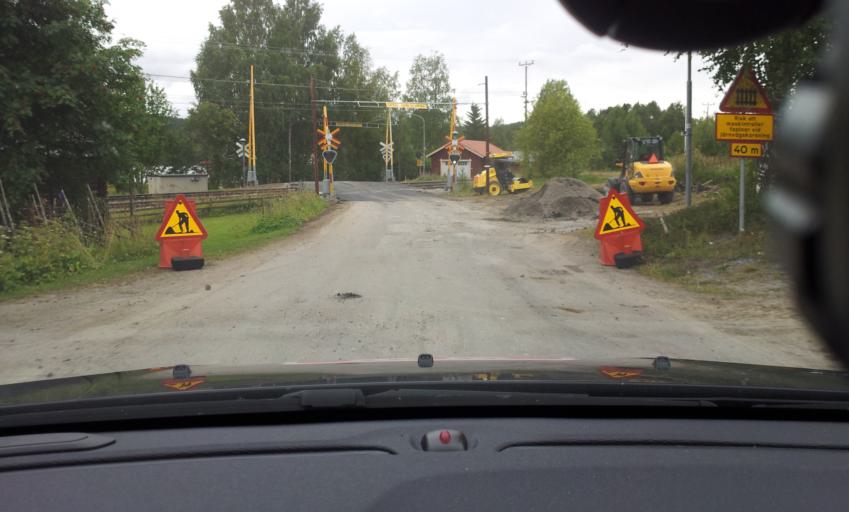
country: SE
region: Jaemtland
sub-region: OEstersunds Kommun
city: Brunflo
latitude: 62.9574
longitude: 15.0364
